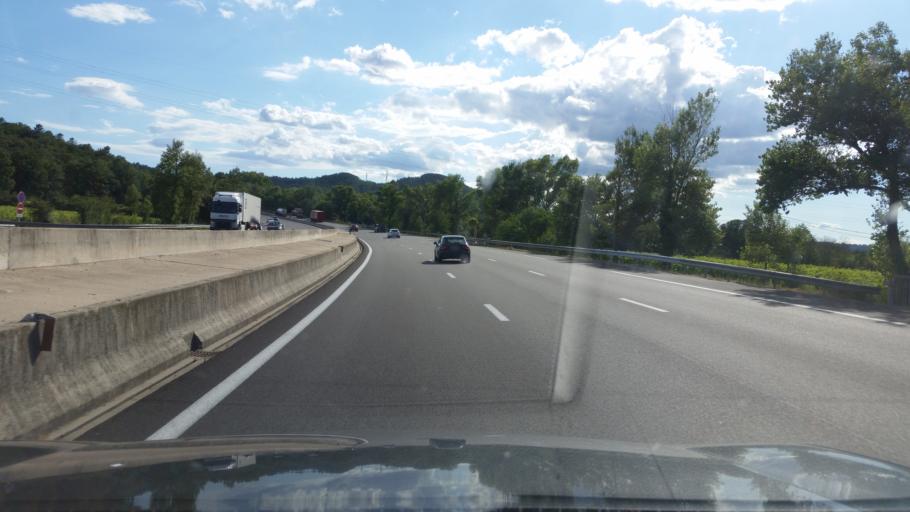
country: FR
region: Provence-Alpes-Cote d'Azur
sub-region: Departement du Var
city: Les Arcs
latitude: 43.4401
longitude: 6.4730
